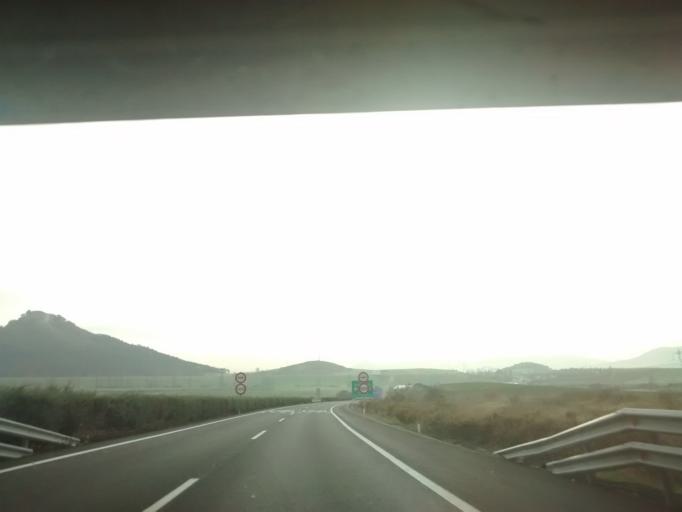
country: ES
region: Navarre
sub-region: Provincia de Navarra
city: Oltza
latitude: 42.8732
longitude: -1.7536
